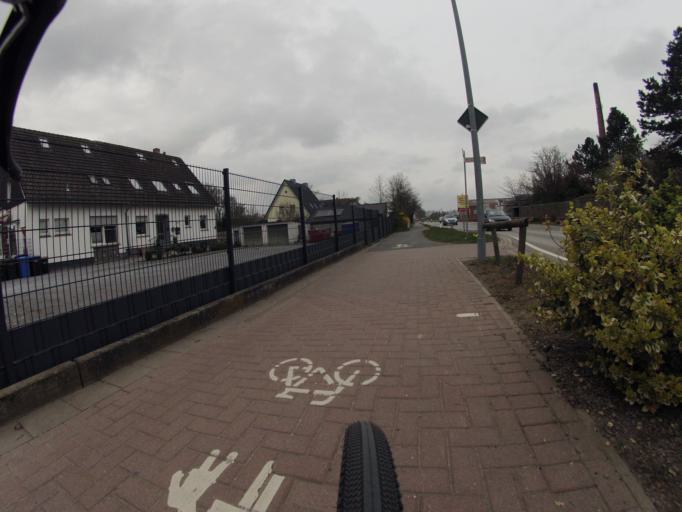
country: DE
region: North Rhine-Westphalia
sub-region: Regierungsbezirk Munster
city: Mettingen
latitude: 52.3385
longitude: 7.7399
